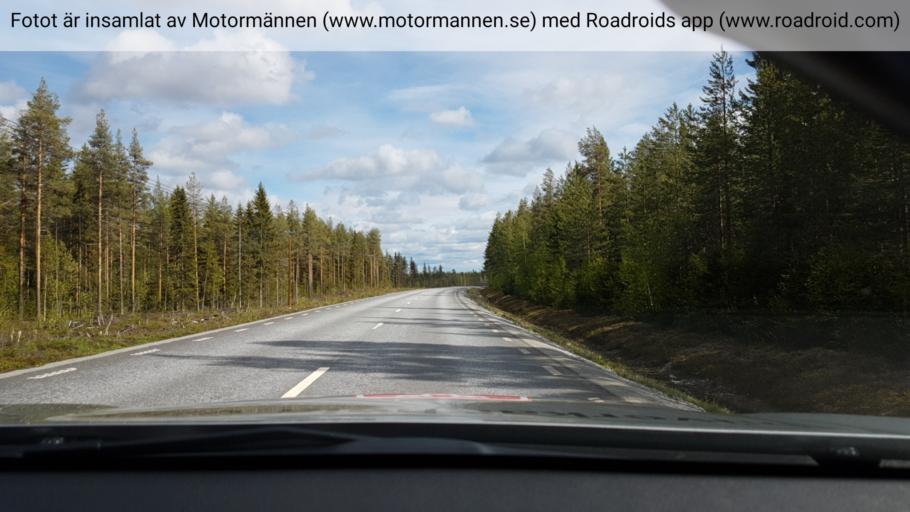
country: SE
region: Vaesterbotten
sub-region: Asele Kommun
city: Insjon
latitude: 64.1270
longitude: 18.0784
